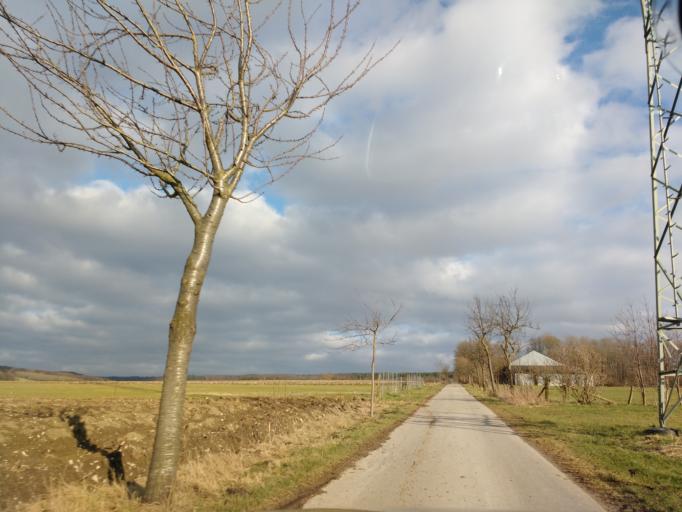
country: DE
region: North Rhine-Westphalia
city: Bad Lippspringe
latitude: 51.7752
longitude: 8.8479
